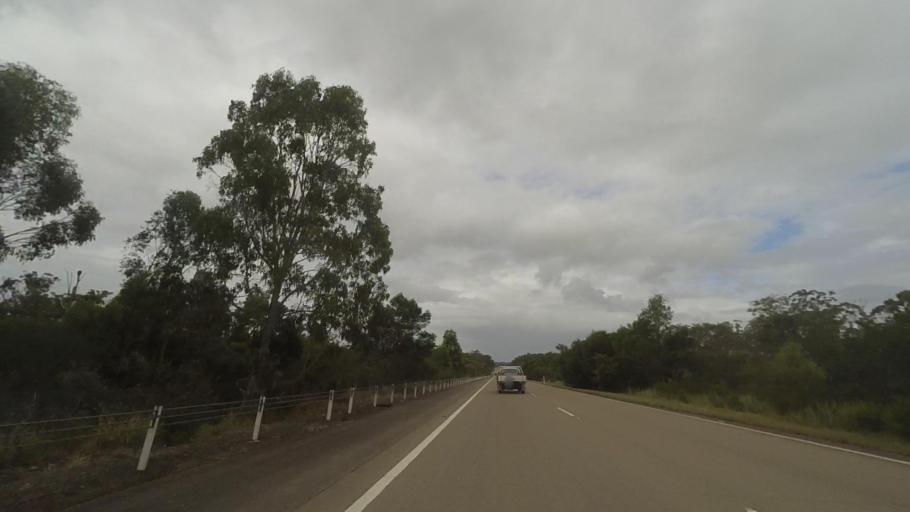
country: AU
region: New South Wales
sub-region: Port Stephens Shire
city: Medowie
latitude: -32.6376
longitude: 151.9333
